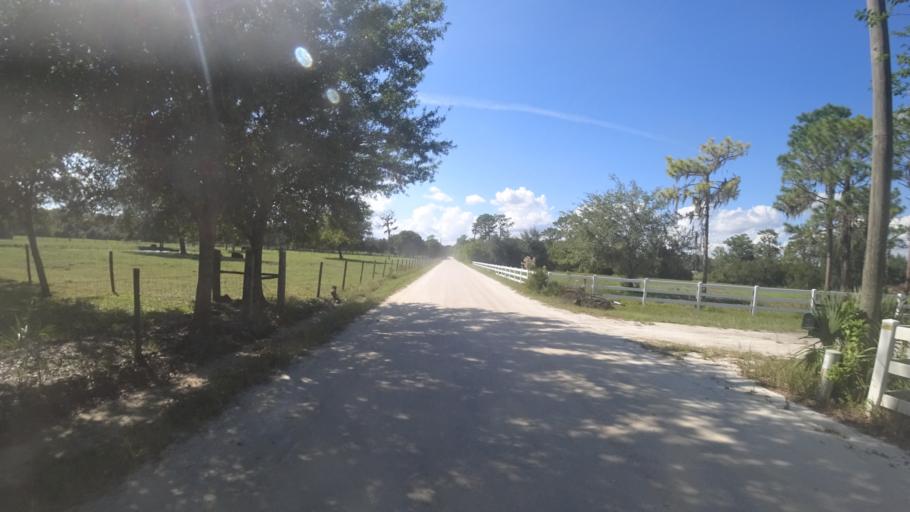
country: US
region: Florida
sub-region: Sarasota County
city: The Meadows
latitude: 27.4526
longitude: -82.2961
